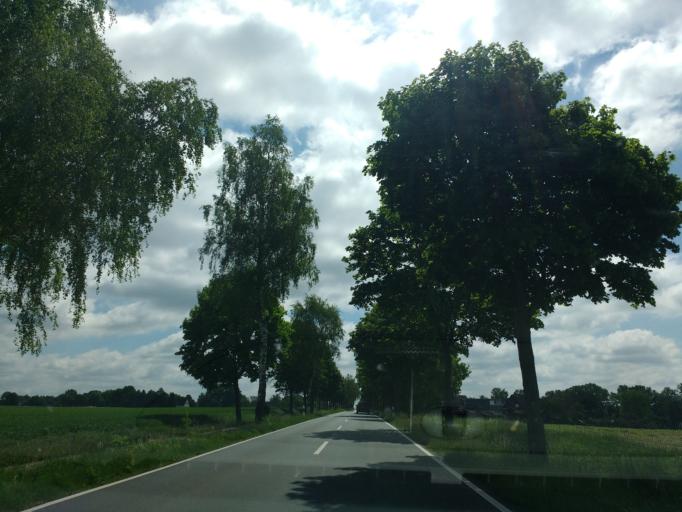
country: DE
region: Lower Saxony
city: Walsrode
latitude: 52.8368
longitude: 9.6275
